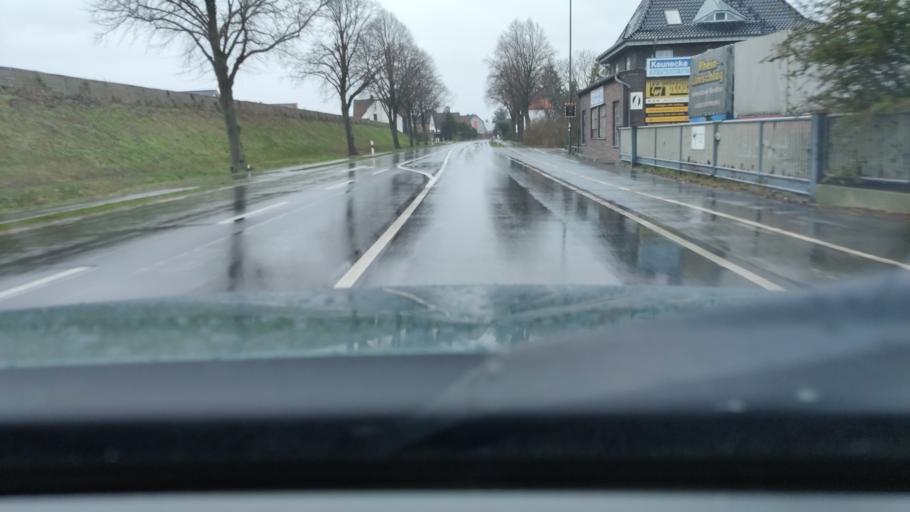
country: DE
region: Lower Saxony
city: Ilsede
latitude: 52.2736
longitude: 10.2244
